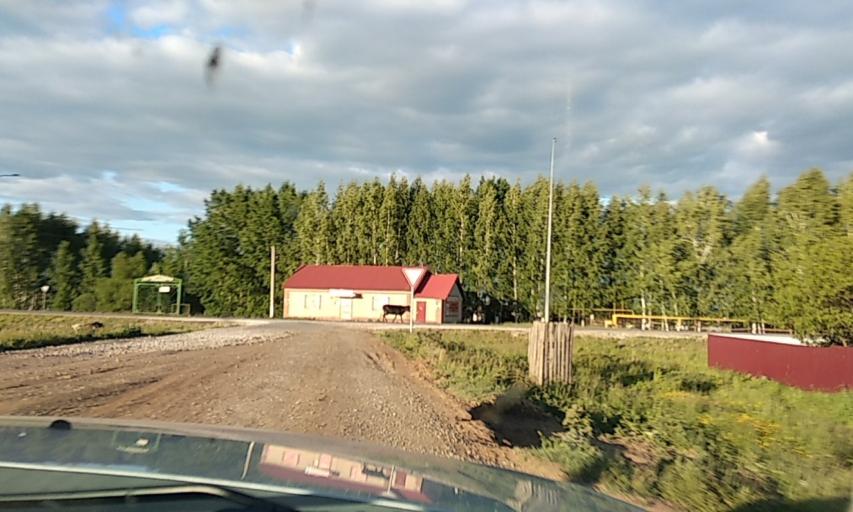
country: RU
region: Tatarstan
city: Nurlat
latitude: 54.8416
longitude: 50.7891
